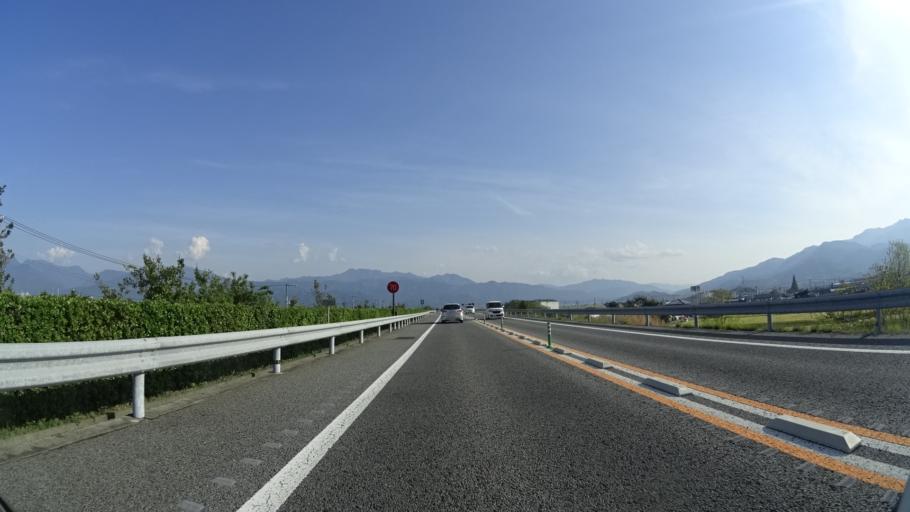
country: JP
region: Ehime
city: Saijo
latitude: 33.9441
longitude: 133.0688
